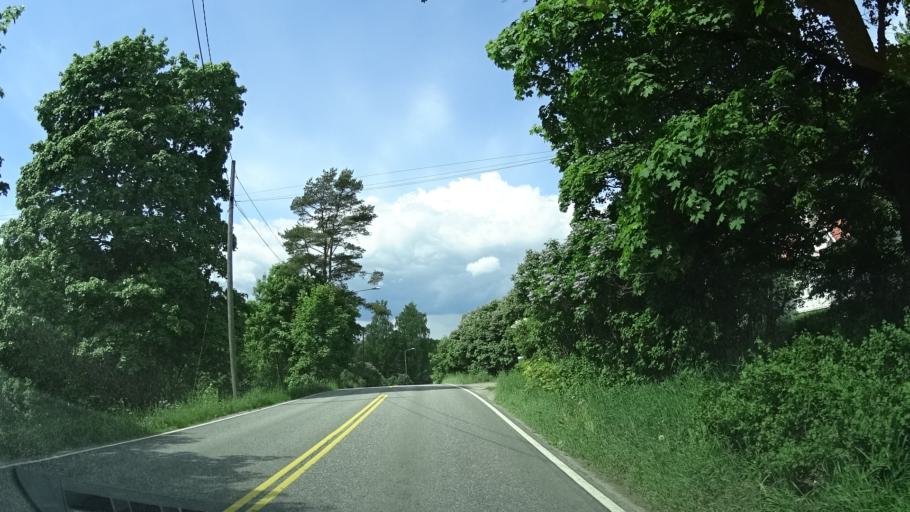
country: FI
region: Uusimaa
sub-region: Helsinki
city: Kirkkonummi
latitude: 60.2216
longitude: 24.4700
